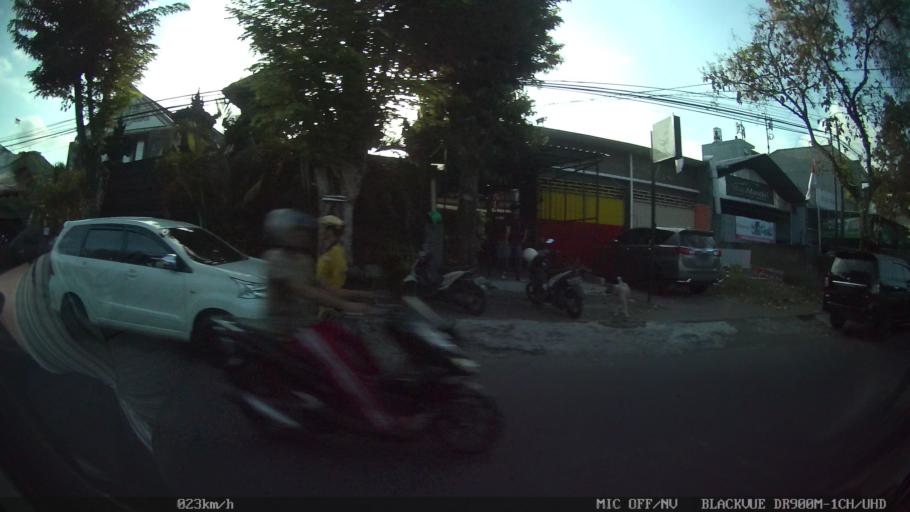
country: ID
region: Bali
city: Banjar Kertasari
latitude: -8.6237
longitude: 115.2092
